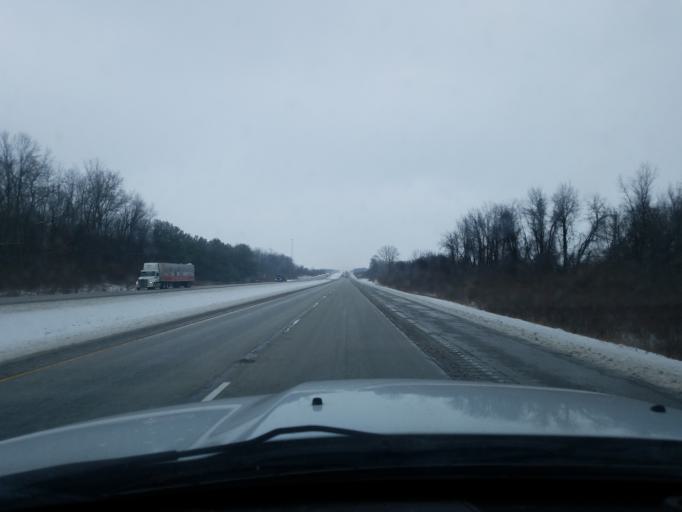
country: US
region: Indiana
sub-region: Fulton County
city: Rochester
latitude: 41.1314
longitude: -86.2397
